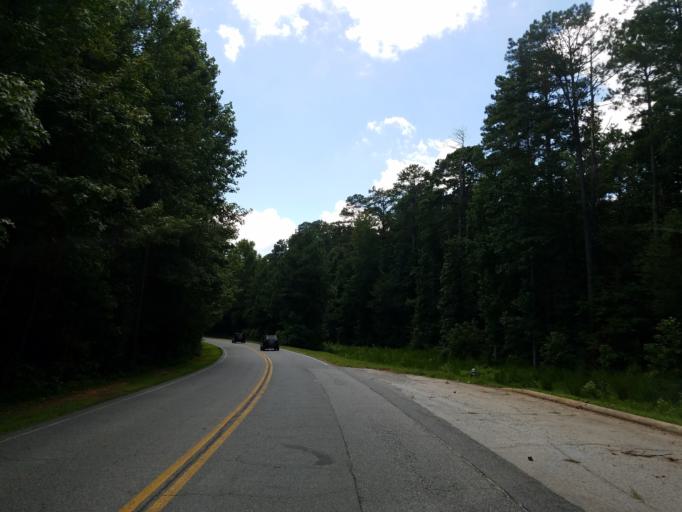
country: US
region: Georgia
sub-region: Fulton County
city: Johns Creek
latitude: 34.1005
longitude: -84.2203
